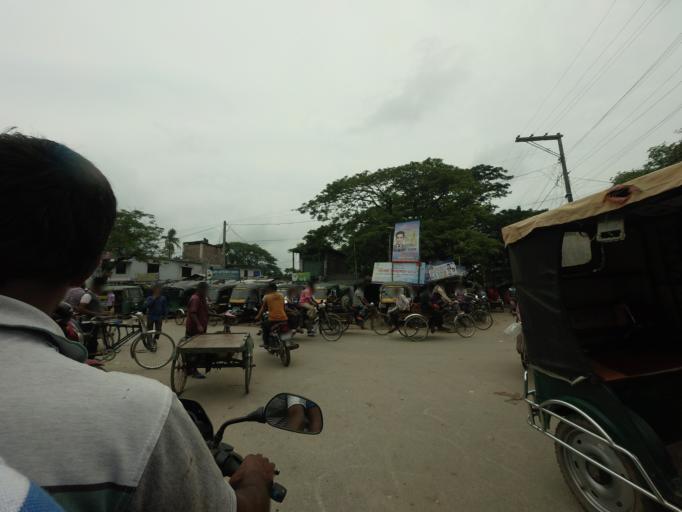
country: BD
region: Khulna
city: Kalia
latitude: 23.1809
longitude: 89.6477
